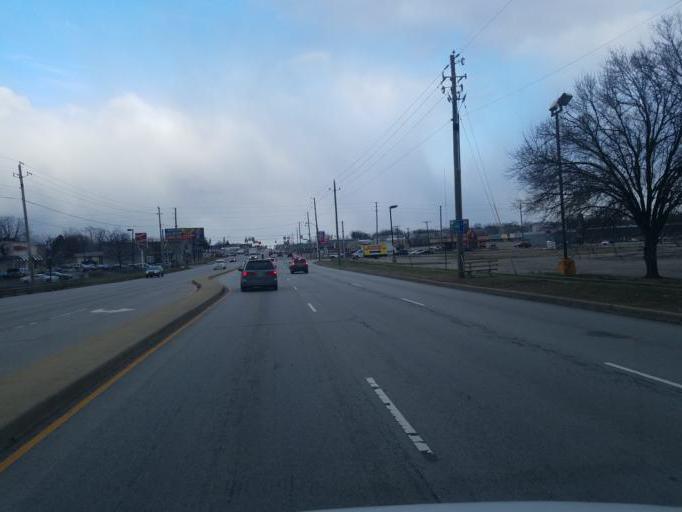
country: US
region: Indiana
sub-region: Marion County
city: Warren Park
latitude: 39.7729
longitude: -86.0280
